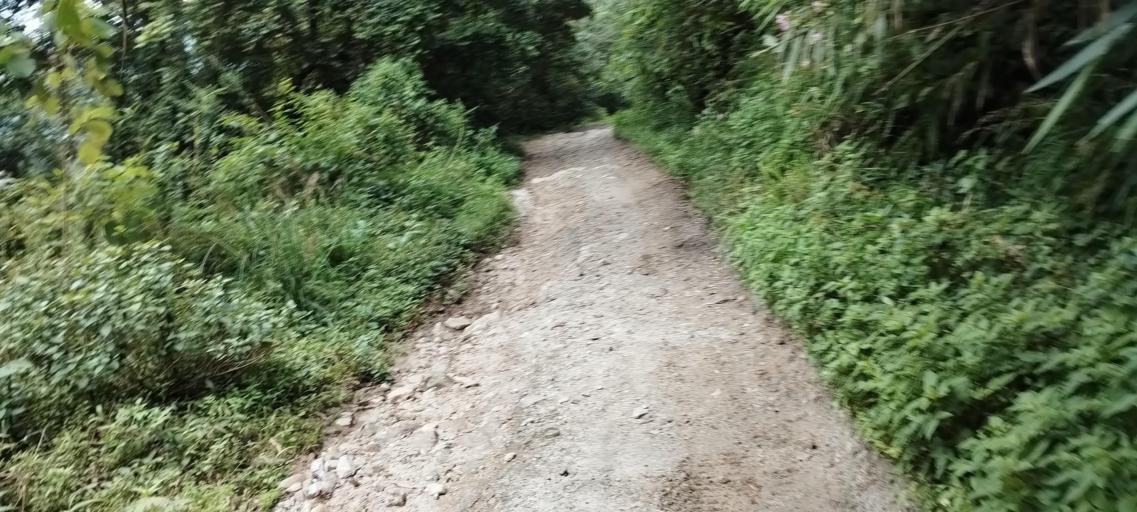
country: NP
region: Central Region
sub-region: Bagmati Zone
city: Kathmandu
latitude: 27.7892
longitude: 85.3764
